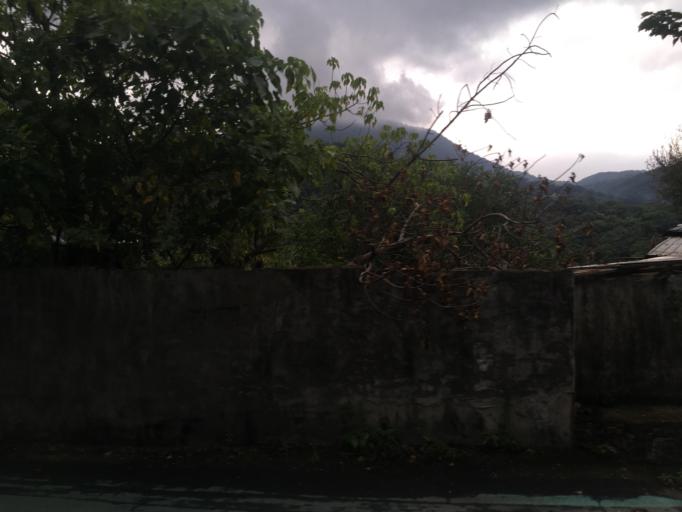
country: TW
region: Taipei
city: Taipei
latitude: 25.1403
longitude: 121.5278
